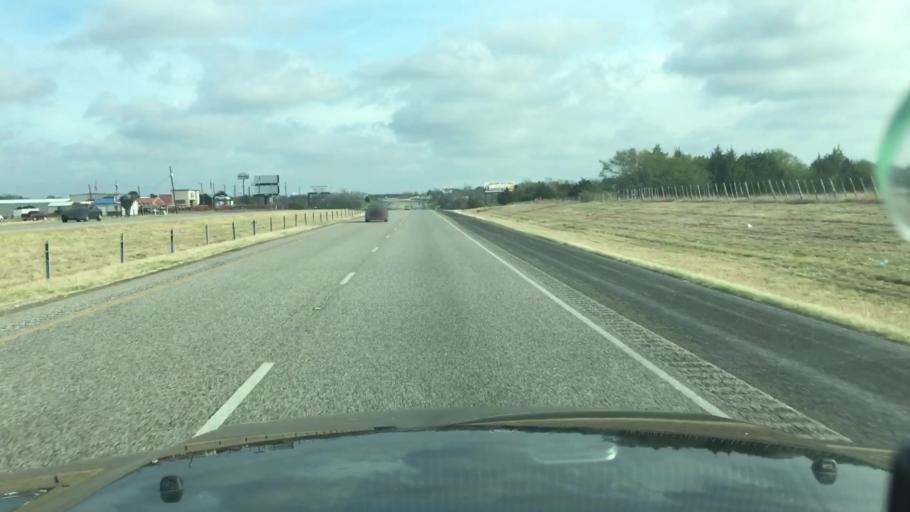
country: US
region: Texas
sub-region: Washington County
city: Brenham
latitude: 30.1399
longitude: -96.2791
